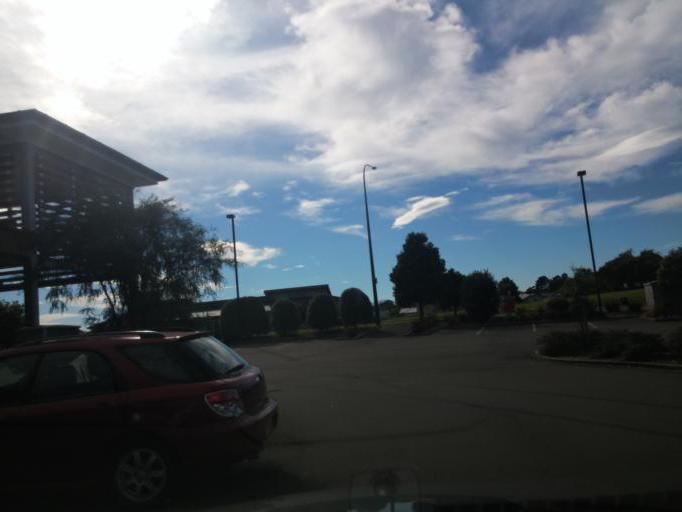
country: NZ
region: Manawatu-Wanganui
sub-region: Palmerston North City
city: Palmerston North
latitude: -40.3873
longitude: 175.6390
